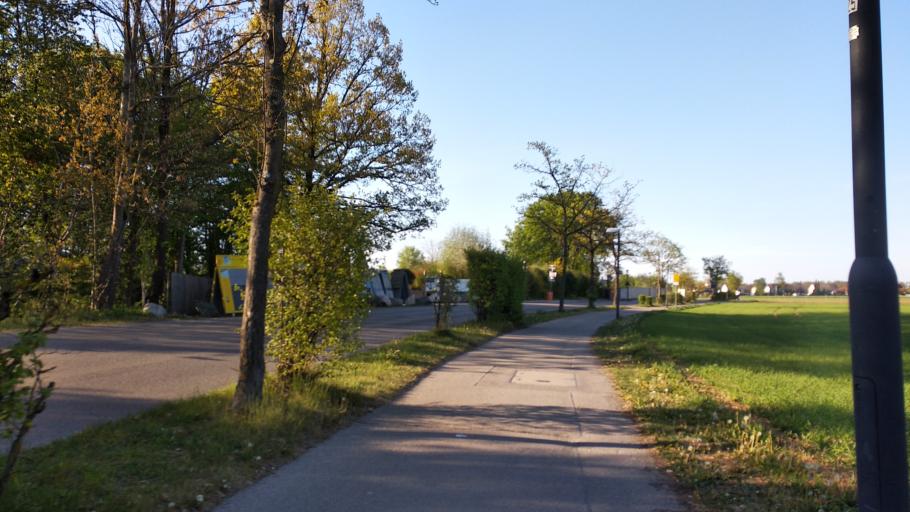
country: DE
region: Bavaria
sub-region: Upper Bavaria
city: Putzbrunn
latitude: 48.0780
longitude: 11.6933
